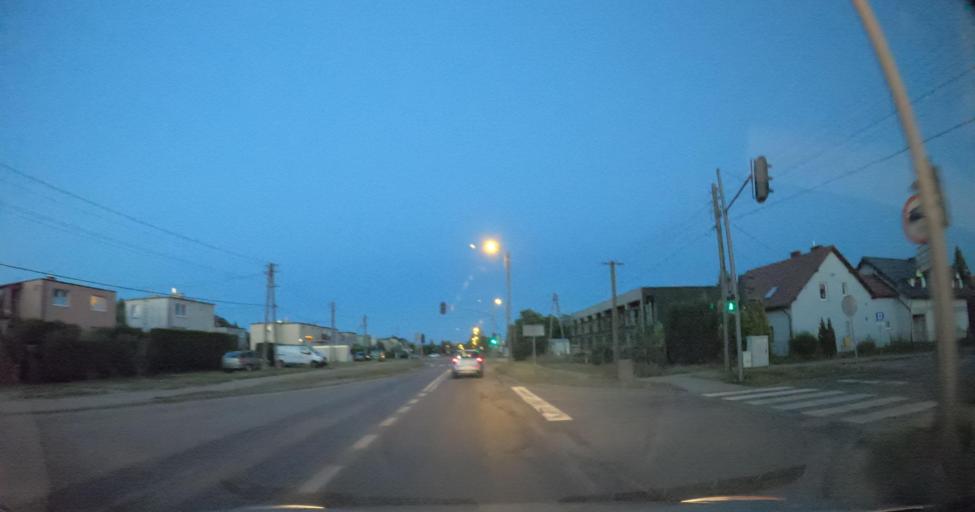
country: PL
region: Pomeranian Voivodeship
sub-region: Gdynia
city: Wielki Kack
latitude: 54.4330
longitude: 18.4720
